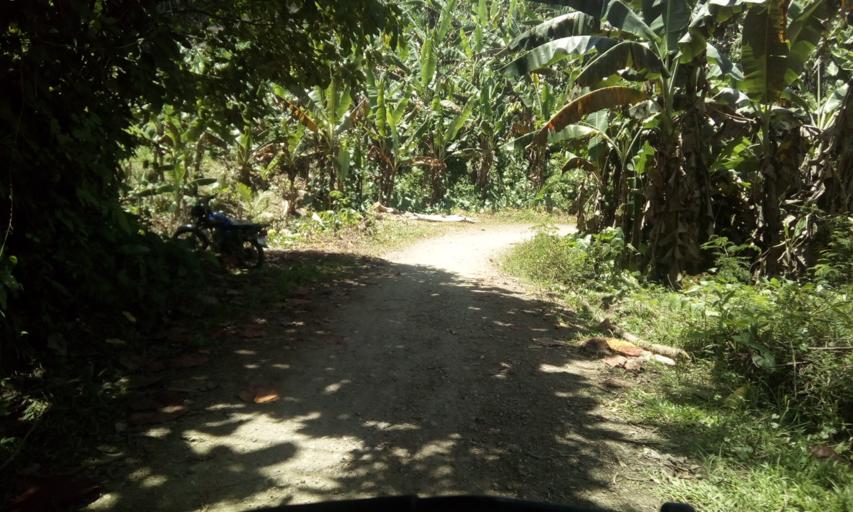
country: PH
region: Caraga
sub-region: Province of Agusan del Sur
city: Santa Josefa
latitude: 7.9545
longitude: 125.9928
